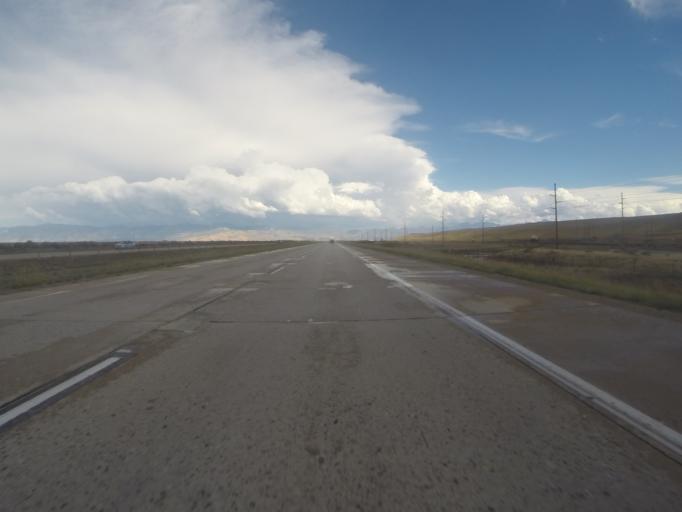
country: US
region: Utah
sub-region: Salt Lake County
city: Magna
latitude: 40.7707
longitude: -112.1246
